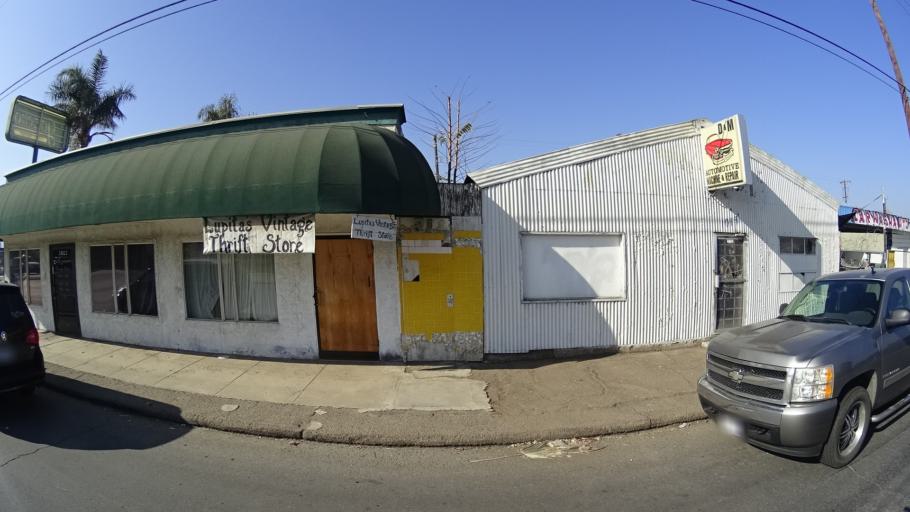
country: US
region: California
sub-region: Kern County
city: Bakersfield
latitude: 35.3442
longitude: -119.0213
